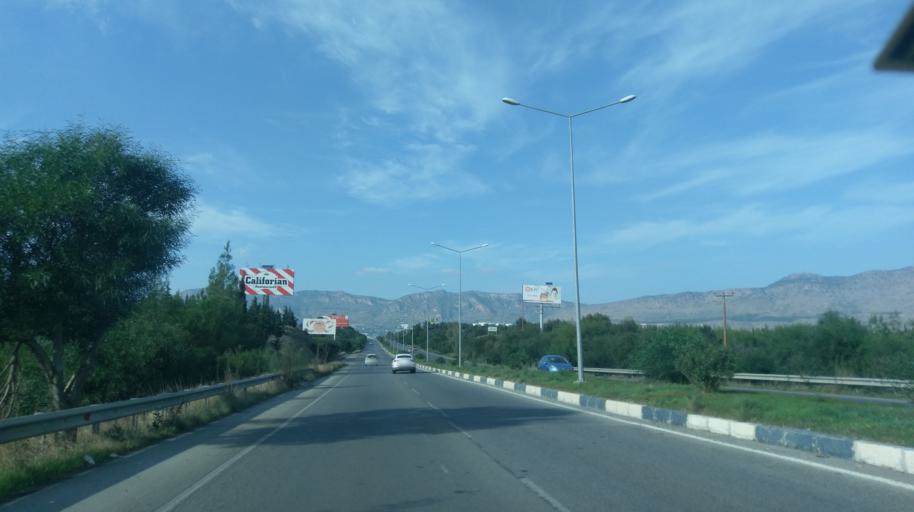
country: CY
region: Lefkosia
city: Nicosia
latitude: 35.2449
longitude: 33.3077
